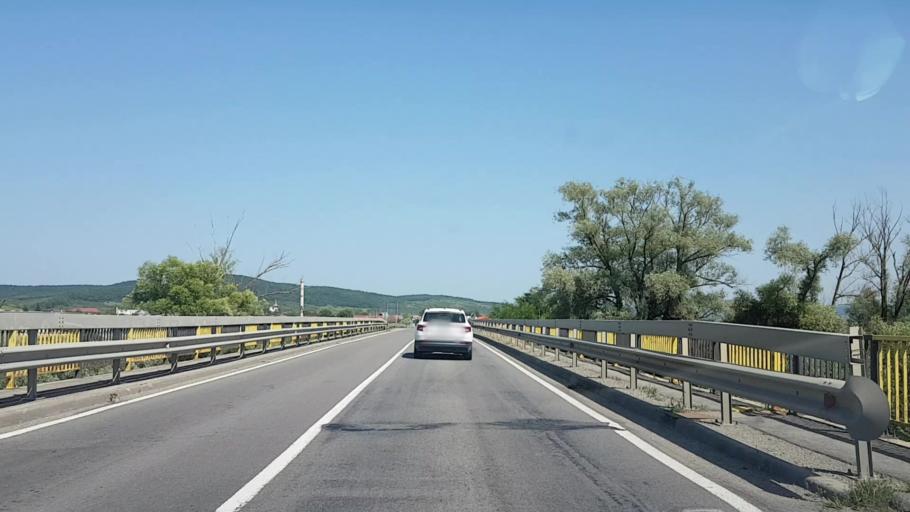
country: RO
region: Bistrita-Nasaud
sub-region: Comuna Sintereag
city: Sintereag
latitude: 47.1797
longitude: 24.2718
